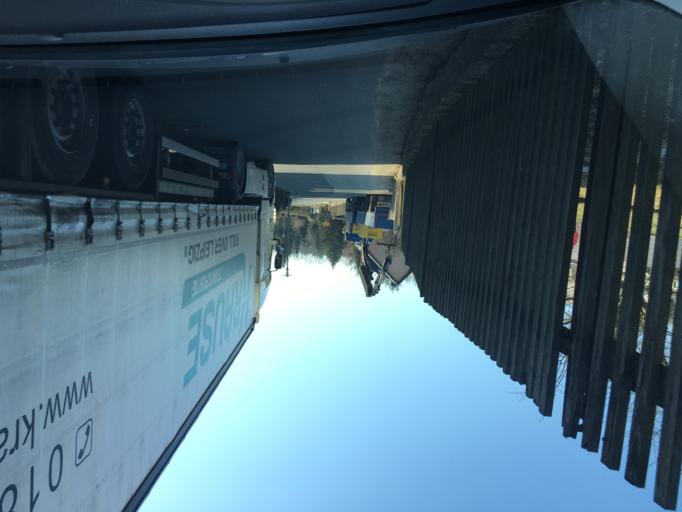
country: DE
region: Saxony
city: Geithain
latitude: 51.0494
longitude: 12.7065
